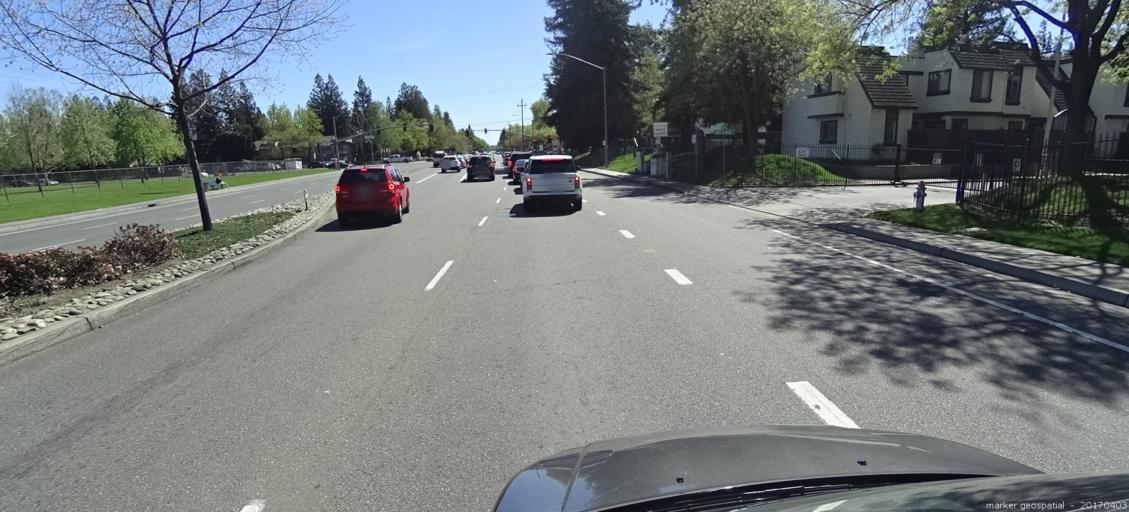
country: US
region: California
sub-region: Sacramento County
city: Sacramento
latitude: 38.6286
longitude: -121.4980
